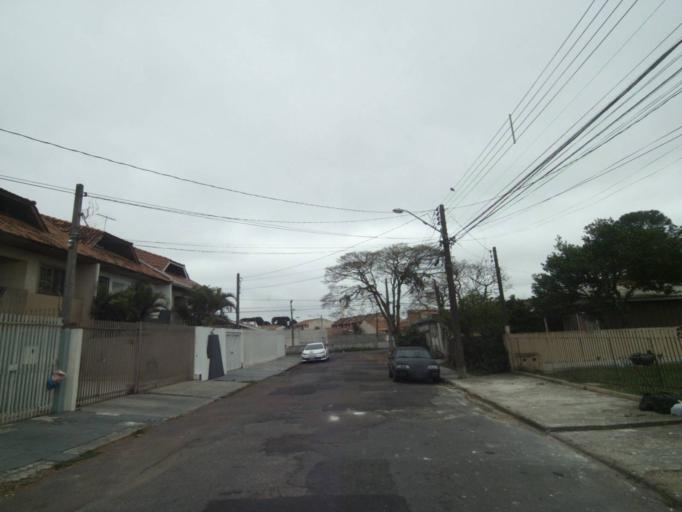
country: BR
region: Parana
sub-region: Curitiba
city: Curitiba
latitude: -25.4662
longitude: -49.2708
